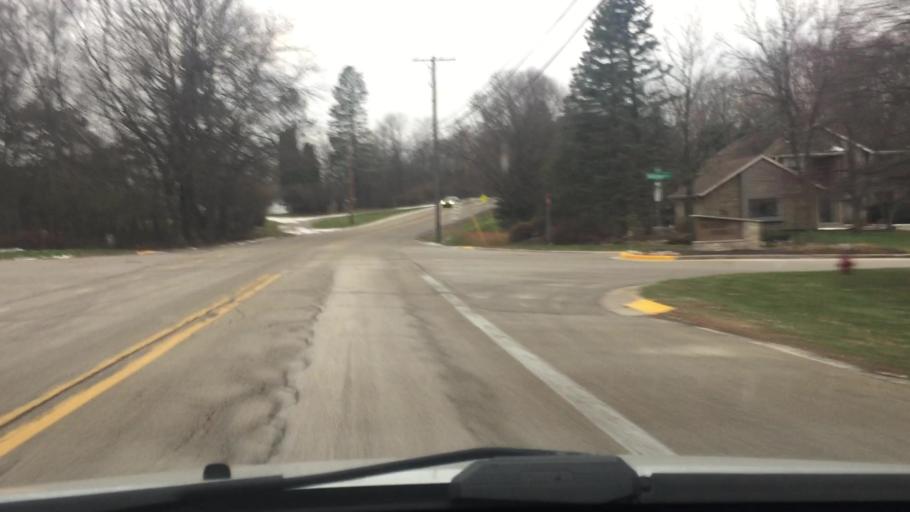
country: US
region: Wisconsin
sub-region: Waukesha County
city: Pewaukee
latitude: 43.0653
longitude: -88.2976
